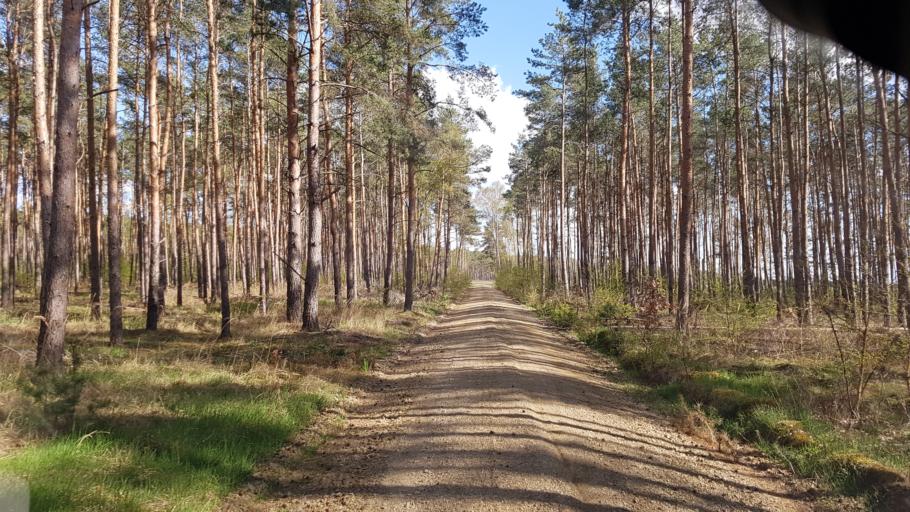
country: DE
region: Brandenburg
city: Muhlberg
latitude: 51.4802
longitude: 13.2866
